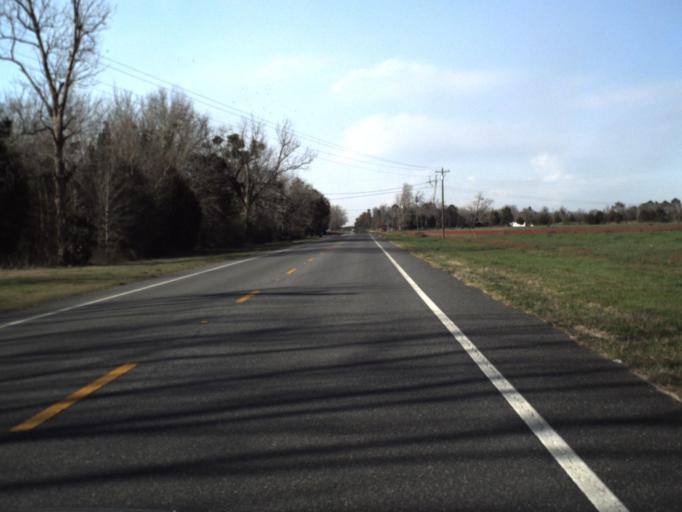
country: US
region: Florida
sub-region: Calhoun County
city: Blountstown
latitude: 30.4839
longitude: -85.2003
